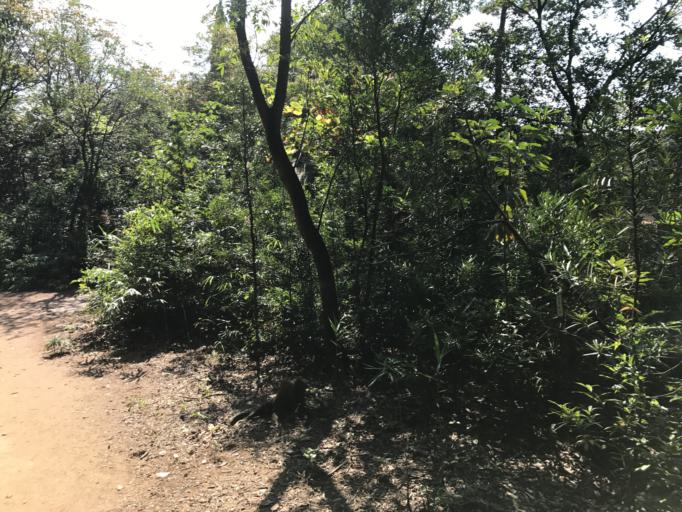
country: JP
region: Fukuoka
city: Sasaguri
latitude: 33.6360
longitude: 130.5058
